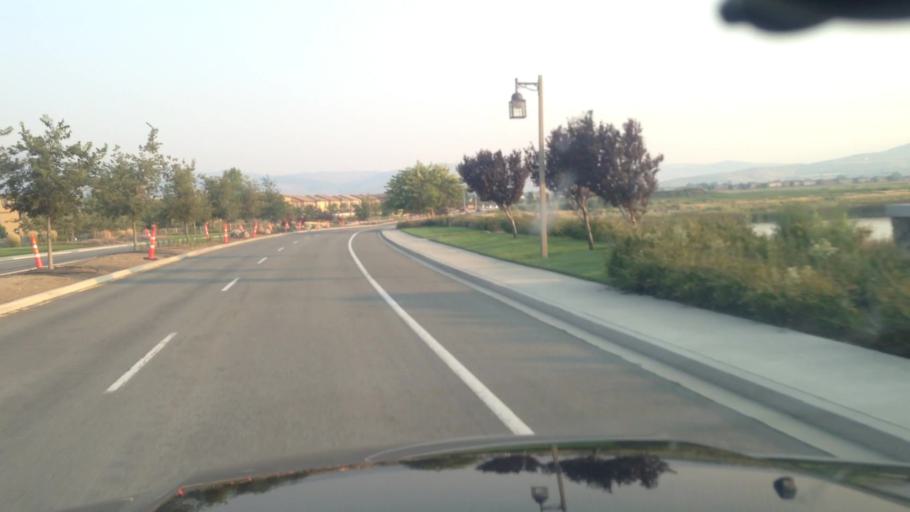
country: US
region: Nevada
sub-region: Washoe County
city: Sparks
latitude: 39.4209
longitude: -119.7327
